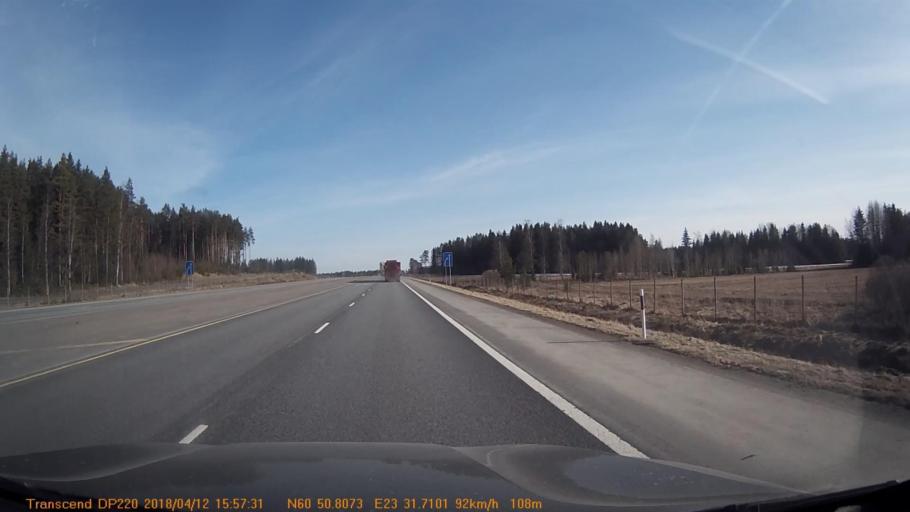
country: FI
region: Haeme
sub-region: Forssa
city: Jokioinen
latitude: 60.8466
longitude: 23.5287
